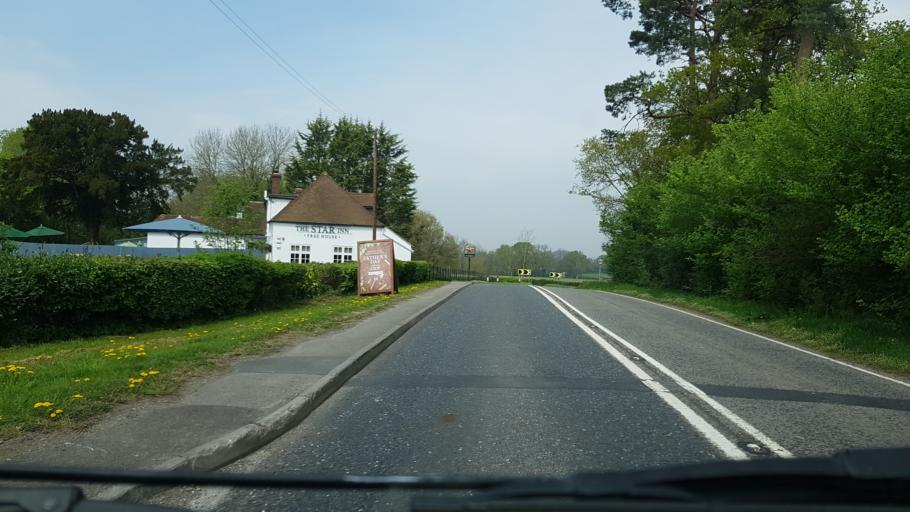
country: GB
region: England
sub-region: Hampshire
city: Kingsclere
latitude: 51.3343
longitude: -1.2584
